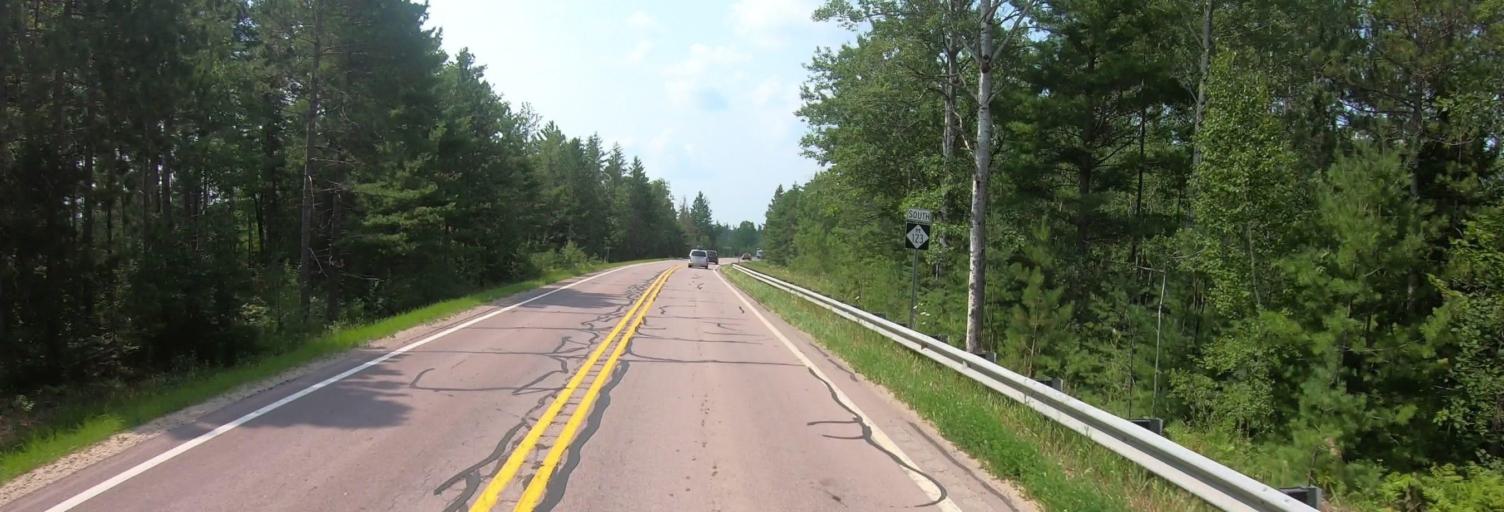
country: US
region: Michigan
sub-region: Luce County
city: Newberry
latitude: 46.4459
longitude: -85.4744
